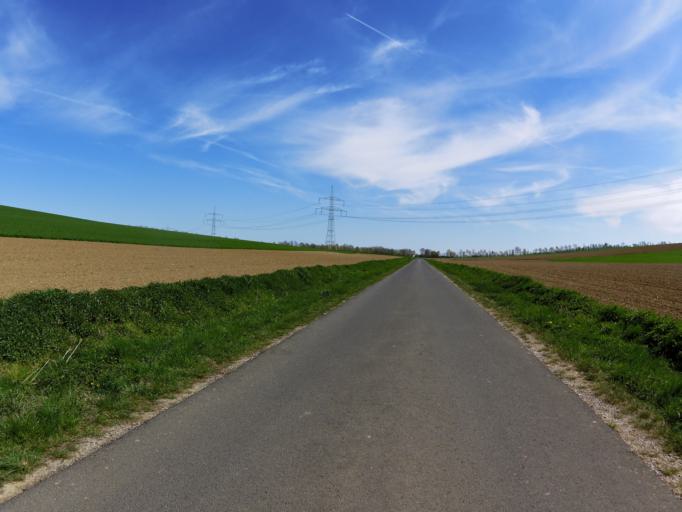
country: DE
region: Bavaria
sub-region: Regierungsbezirk Unterfranken
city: Rottendorf
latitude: 49.7902
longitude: 10.0499
